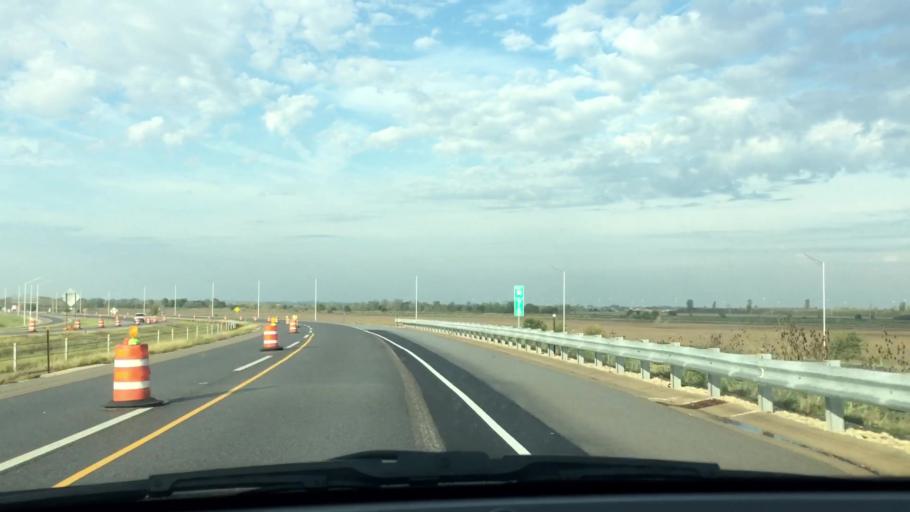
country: US
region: Illinois
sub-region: Ogle County
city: Rochelle
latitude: 41.9006
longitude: -89.0708
